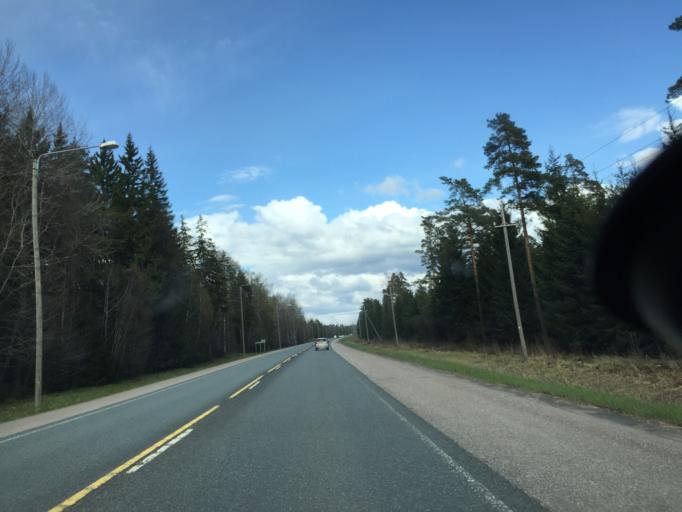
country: FI
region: Uusimaa
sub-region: Raaseporin
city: Ekenaes
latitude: 59.9975
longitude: 23.5102
